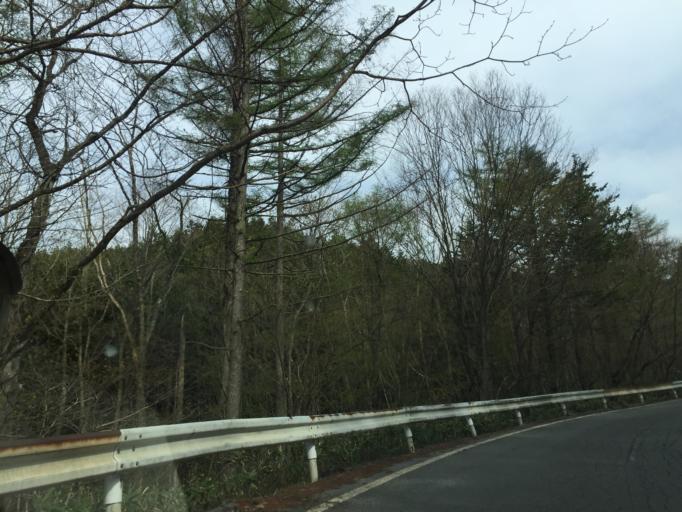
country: JP
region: Gifu
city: Nakatsugawa
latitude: 35.3012
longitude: 137.6664
